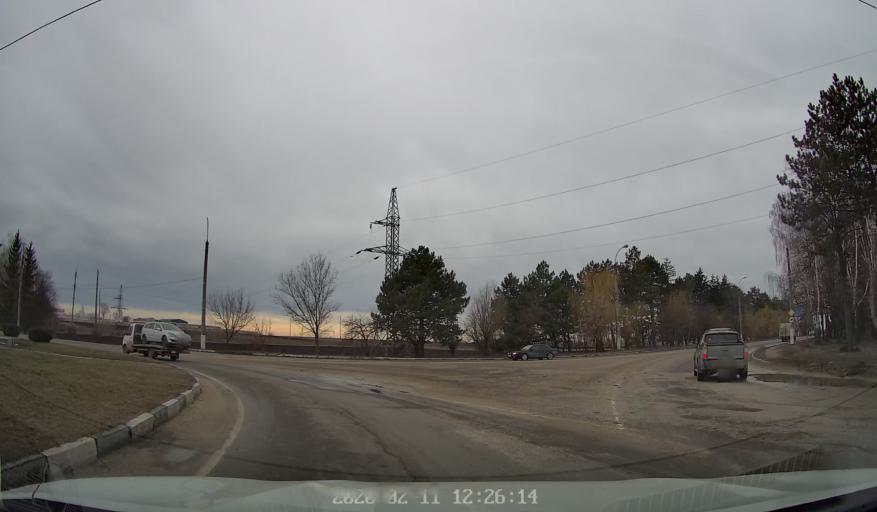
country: MD
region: Raionul Edinet
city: Edinet
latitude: 48.1592
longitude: 27.3300
